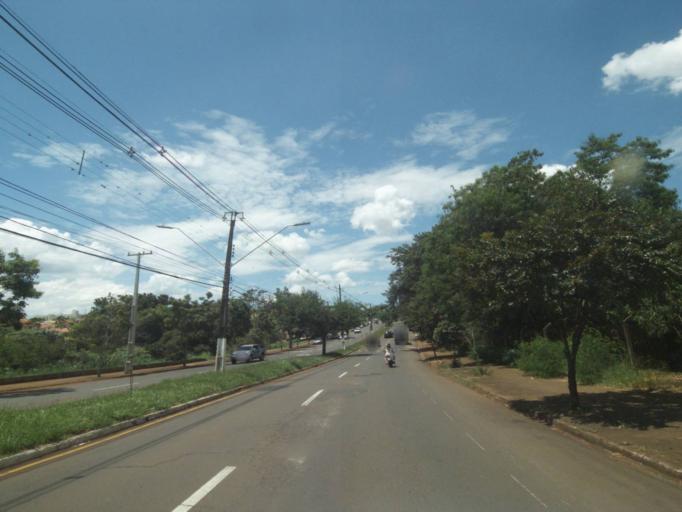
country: BR
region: Parana
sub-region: Londrina
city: Londrina
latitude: -23.3123
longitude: -51.2063
